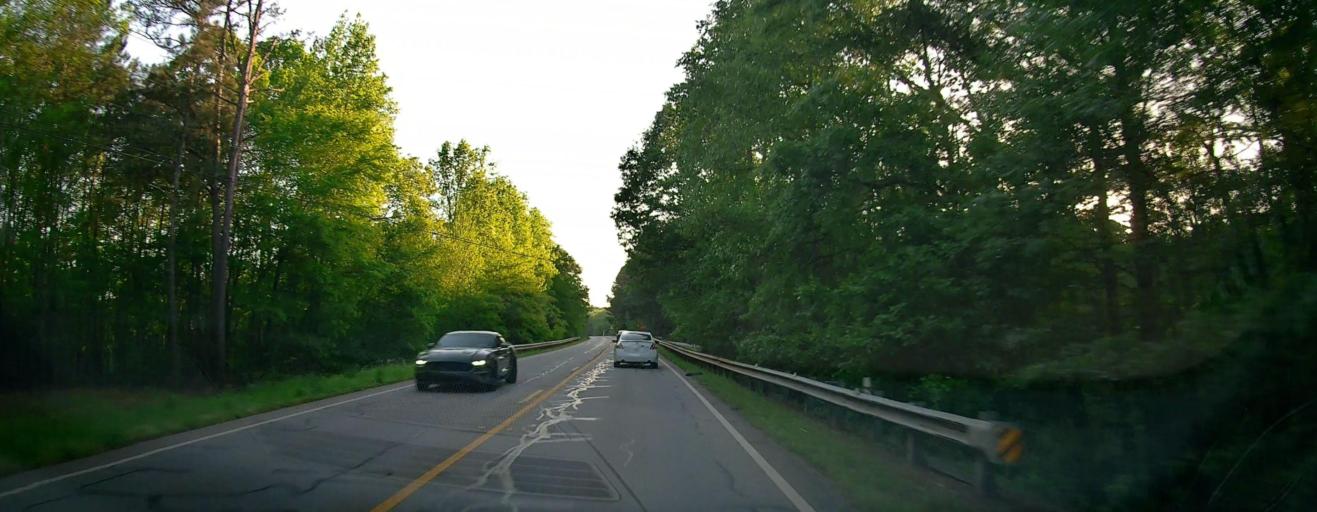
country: US
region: Georgia
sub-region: Newton County
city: Porterdale
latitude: 33.5540
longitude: -83.9291
